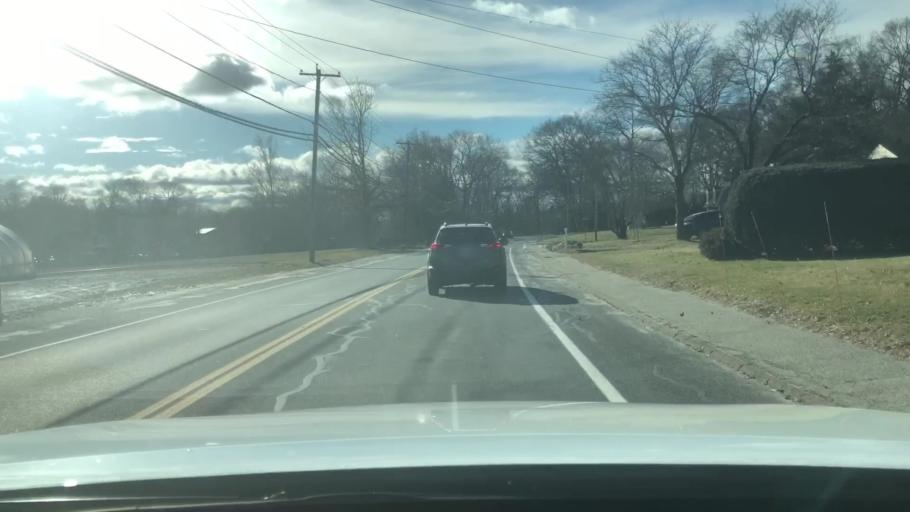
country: US
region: Massachusetts
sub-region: Norfolk County
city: Bellingham
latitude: 42.0433
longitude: -71.4876
